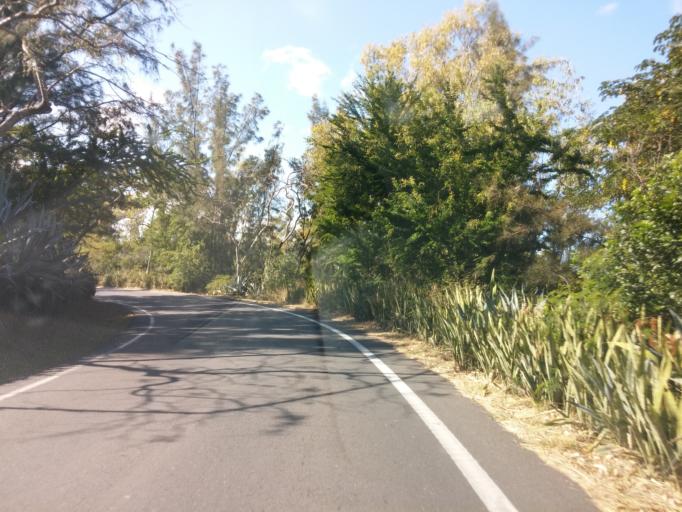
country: RE
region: Reunion
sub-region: Reunion
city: Les Avirons
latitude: -21.2608
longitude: 55.3505
